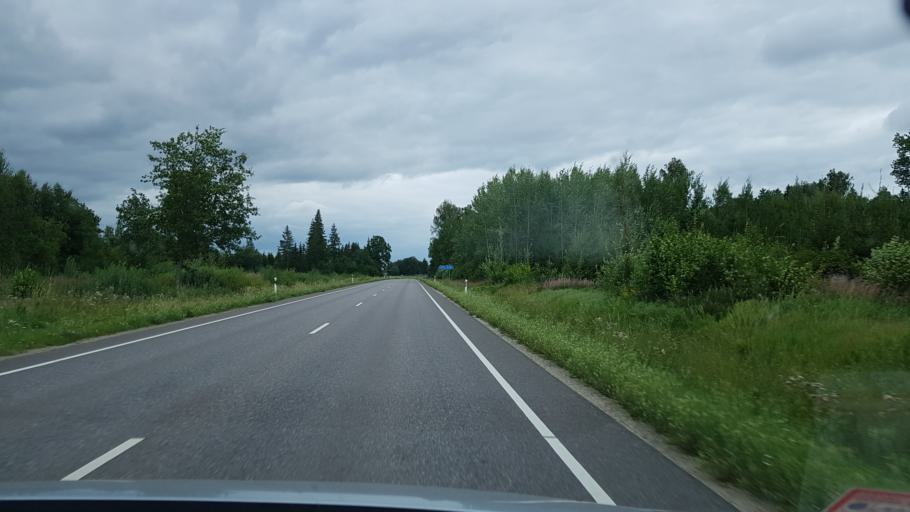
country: EE
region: Tartu
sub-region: Tartu linn
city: Tartu
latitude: 58.4396
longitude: 26.8233
